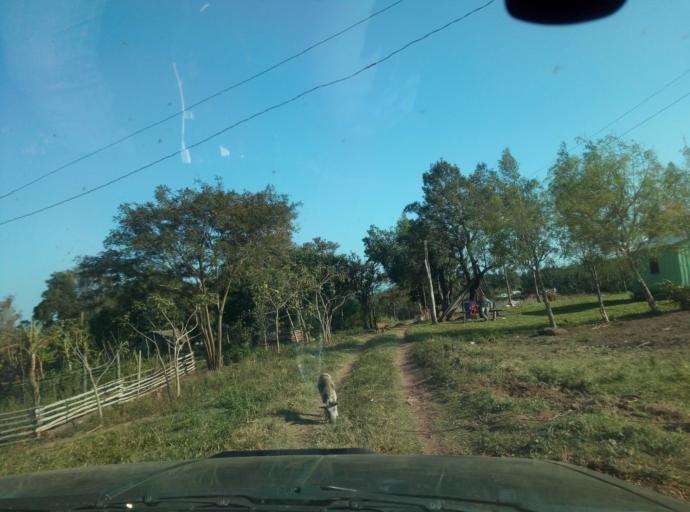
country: PY
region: Caaguazu
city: San Joaquin
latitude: -25.1678
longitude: -56.1174
